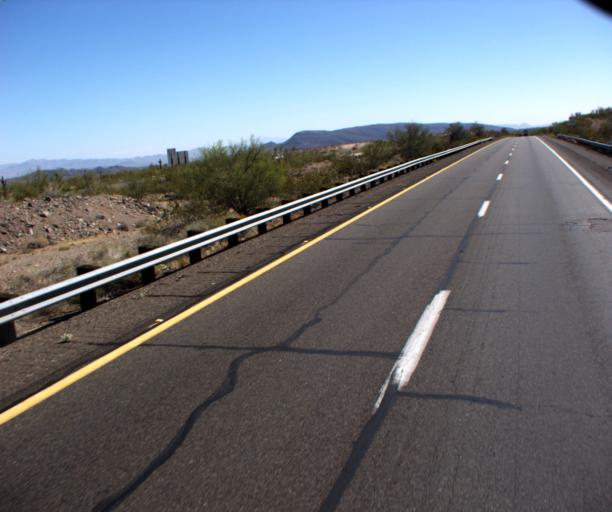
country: US
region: Arizona
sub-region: La Paz County
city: Quartzsite
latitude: 33.6609
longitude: -114.0062
